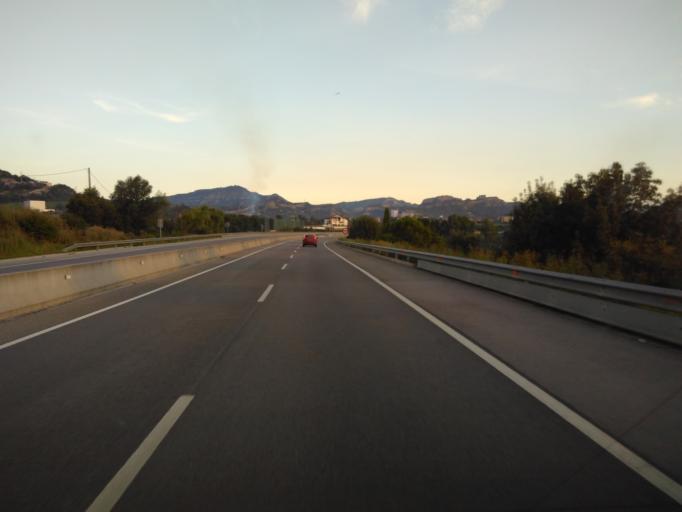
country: ES
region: Catalonia
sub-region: Provincia de Barcelona
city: Santa Cecilia de Voltrega
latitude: 42.0256
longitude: 2.2421
